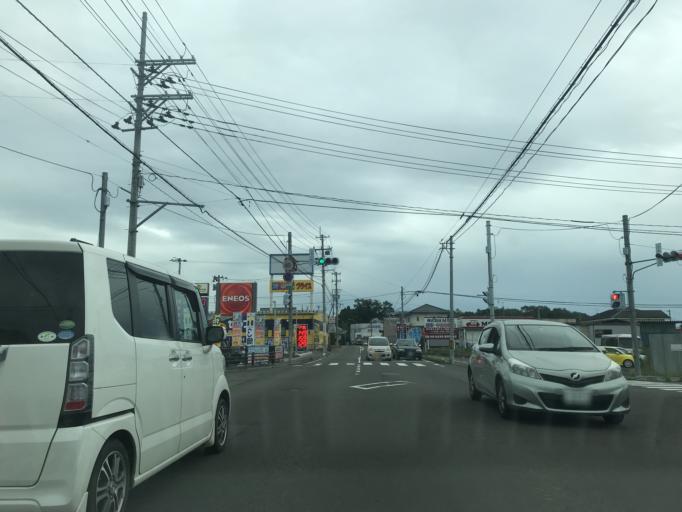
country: JP
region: Miyagi
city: Sendai-shi
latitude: 38.3254
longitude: 140.8618
